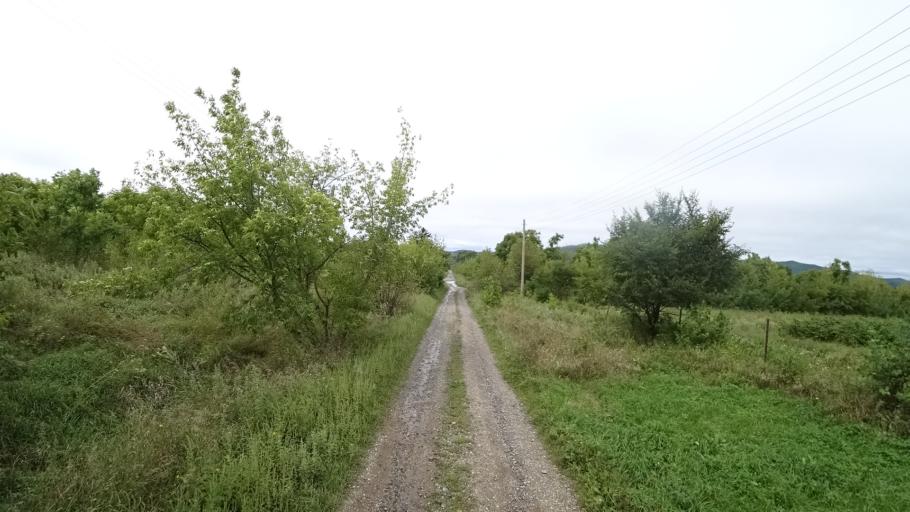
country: RU
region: Primorskiy
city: Lyalichi
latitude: 44.0776
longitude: 132.4828
